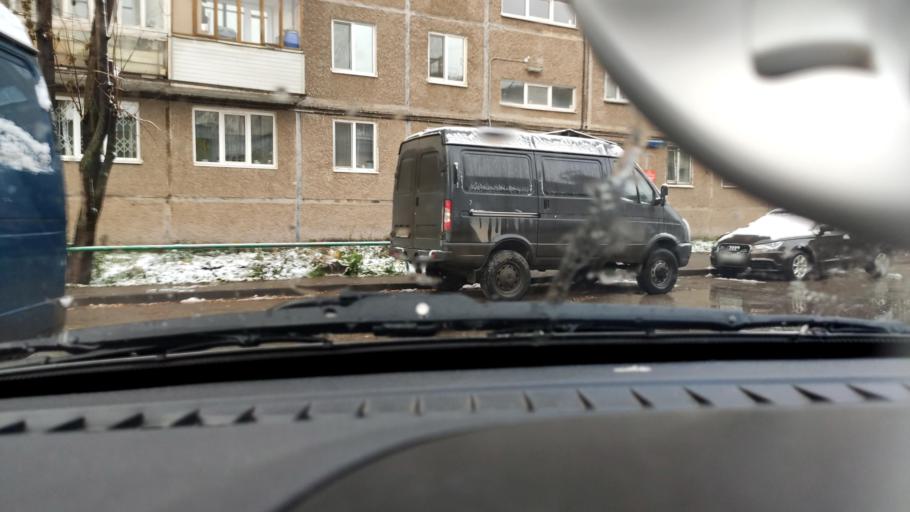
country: RU
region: Perm
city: Kondratovo
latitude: 57.9647
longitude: 56.1790
